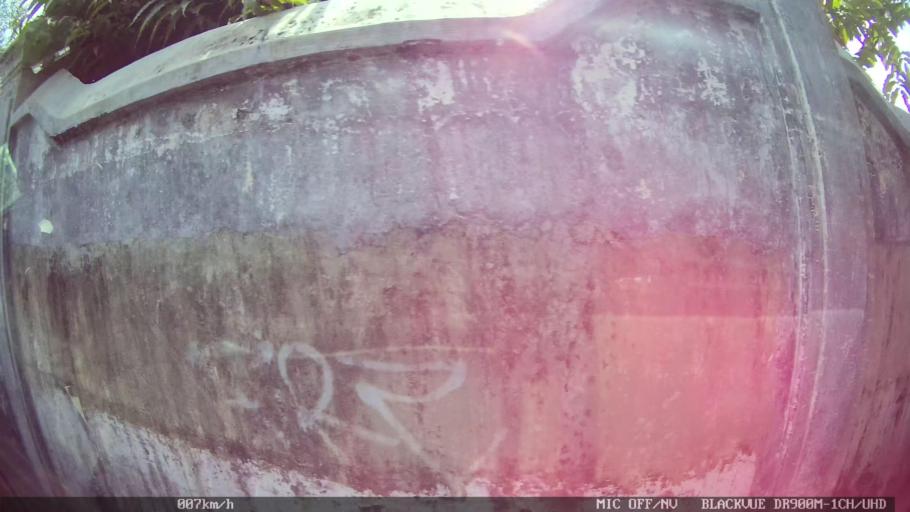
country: ID
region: Daerah Istimewa Yogyakarta
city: Yogyakarta
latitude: -7.8035
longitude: 110.3836
